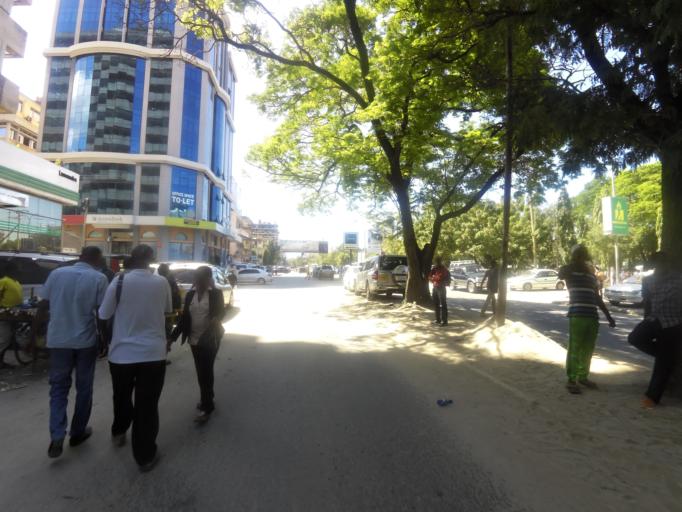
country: TZ
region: Dar es Salaam
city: Dar es Salaam
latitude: -6.8221
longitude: 39.2801
